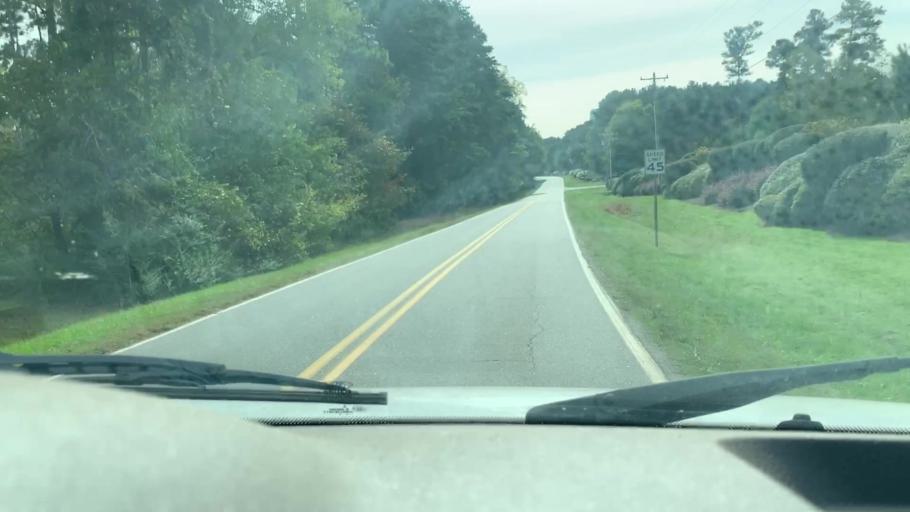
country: US
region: North Carolina
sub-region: Catawba County
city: Lake Norman of Catawba
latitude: 35.5723
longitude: -80.9361
